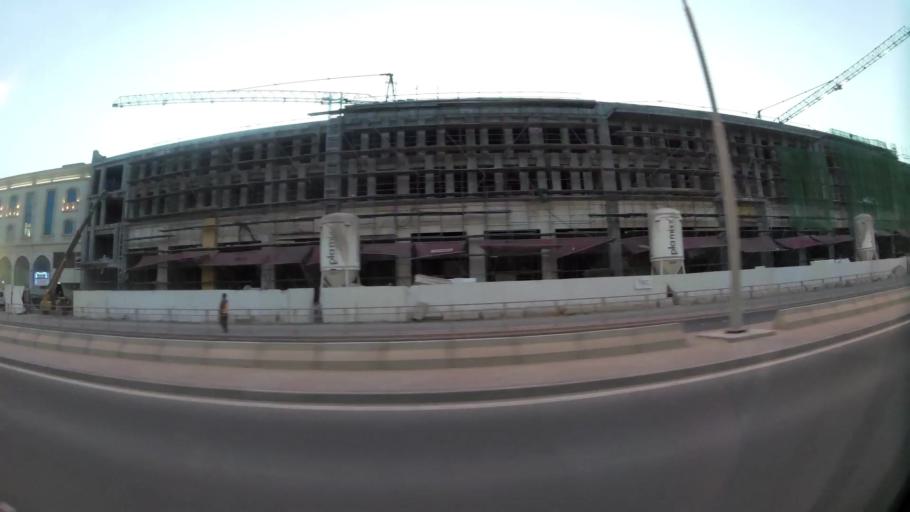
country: QA
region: Al Wakrah
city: Al Wakrah
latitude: 25.1648
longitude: 51.5977
